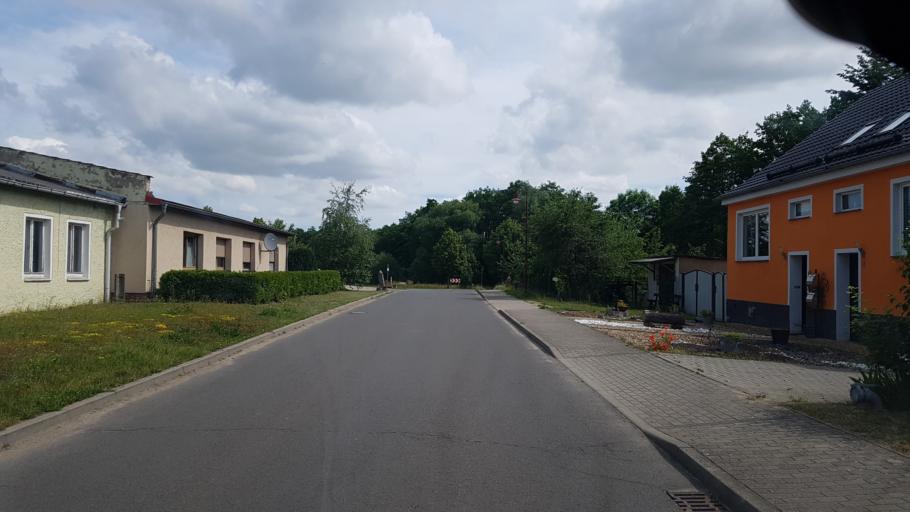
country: DE
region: Mecklenburg-Vorpommern
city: Strasburg
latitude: 53.4357
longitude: 13.7080
